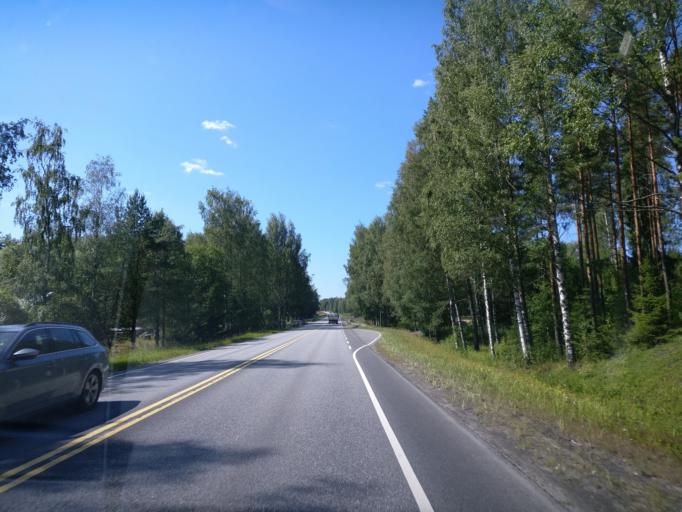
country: FI
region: Satakunta
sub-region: Pori
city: Kullaa
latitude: 61.4611
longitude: 22.1292
